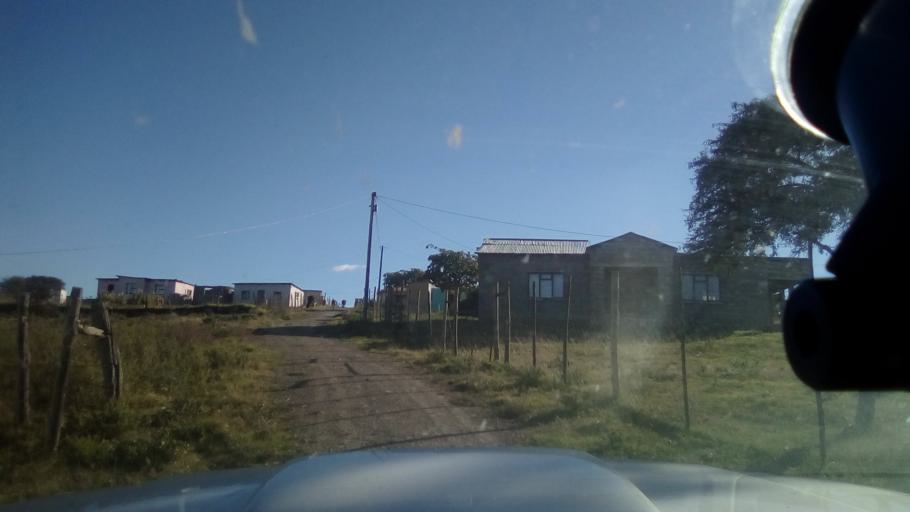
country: ZA
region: Eastern Cape
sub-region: Buffalo City Metropolitan Municipality
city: Bhisho
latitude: -32.7443
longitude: 27.3533
